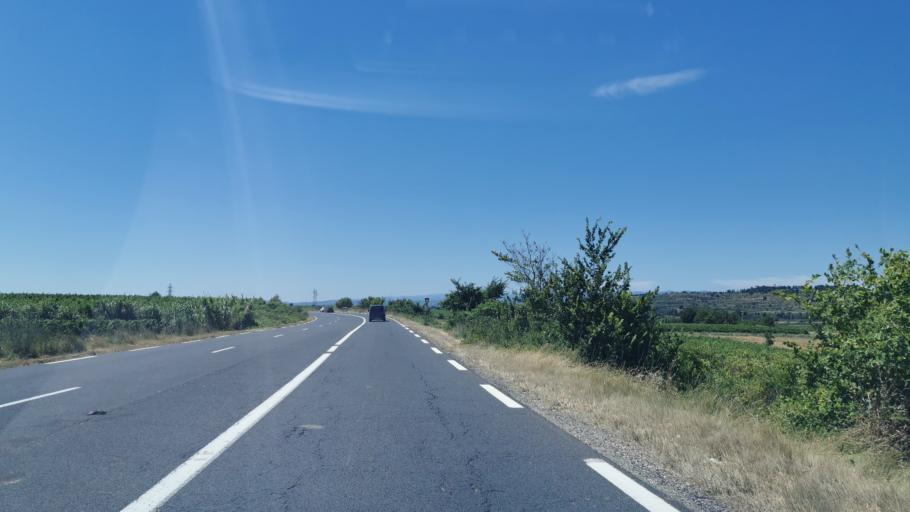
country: FR
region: Languedoc-Roussillon
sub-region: Departement de l'Herault
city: Nissan-lez-Enserune
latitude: 43.2951
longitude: 3.1379
